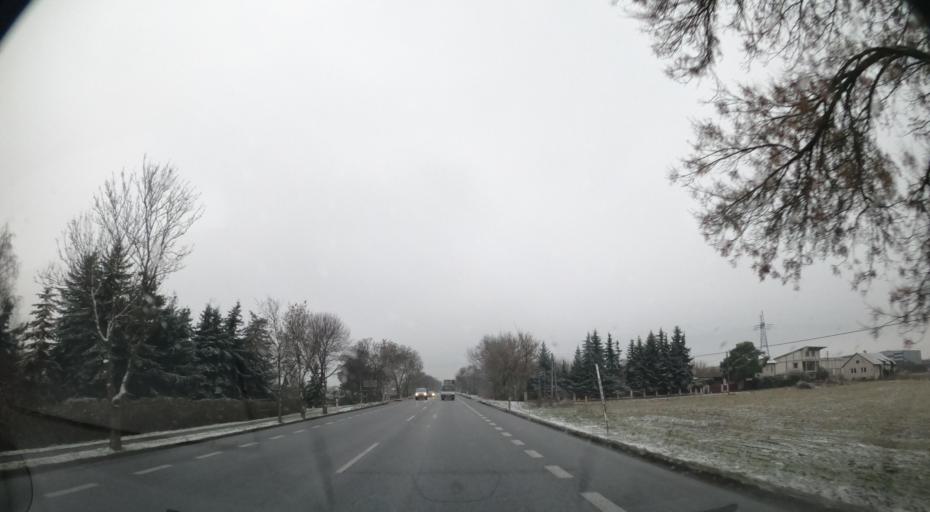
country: PL
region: Masovian Voivodeship
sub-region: Powiat warszawski zachodni
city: Blonie
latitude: 52.1994
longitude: 20.5962
